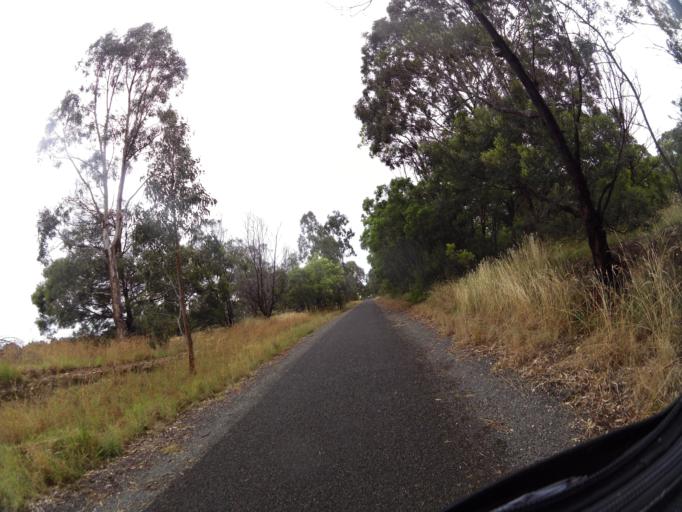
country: AU
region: Victoria
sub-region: East Gippsland
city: Bairnsdale
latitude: -37.8197
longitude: 147.7206
